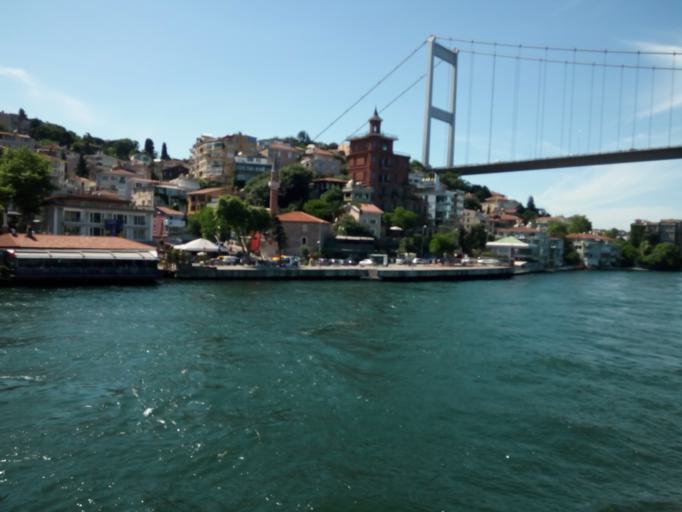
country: TR
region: Istanbul
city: UEskuedar
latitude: 41.0878
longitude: 29.0580
